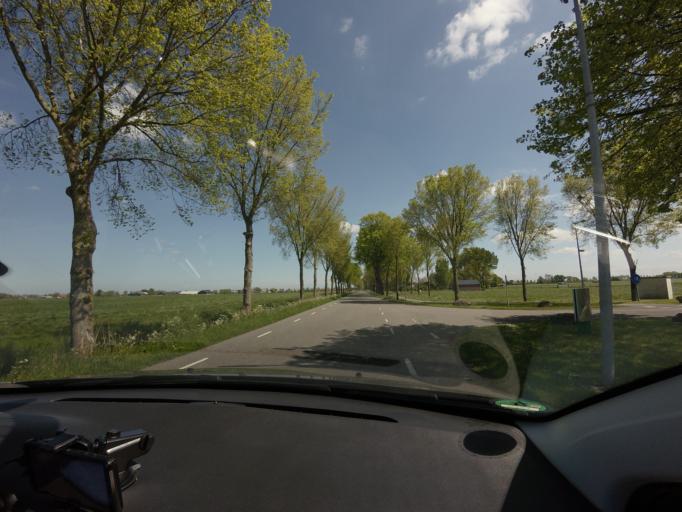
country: NL
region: North Holland
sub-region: Gemeente Beemster
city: Halfweg
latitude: 52.5567
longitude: 4.8759
